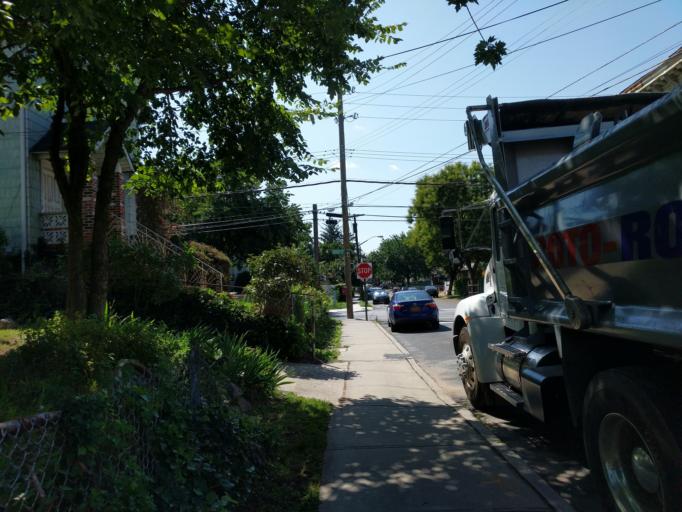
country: US
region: New Jersey
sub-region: Hudson County
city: Bayonne
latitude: 40.6324
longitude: -74.1217
